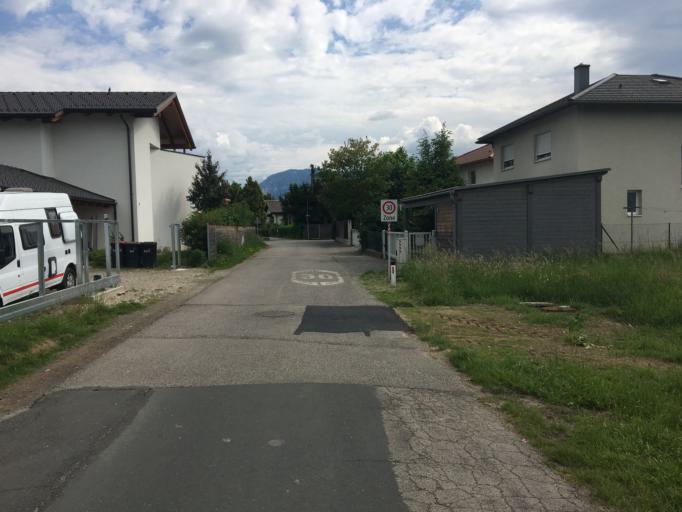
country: AT
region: Carinthia
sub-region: Klagenfurt am Woerthersee
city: Klagenfurt am Woerthersee
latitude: 46.6004
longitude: 14.2723
